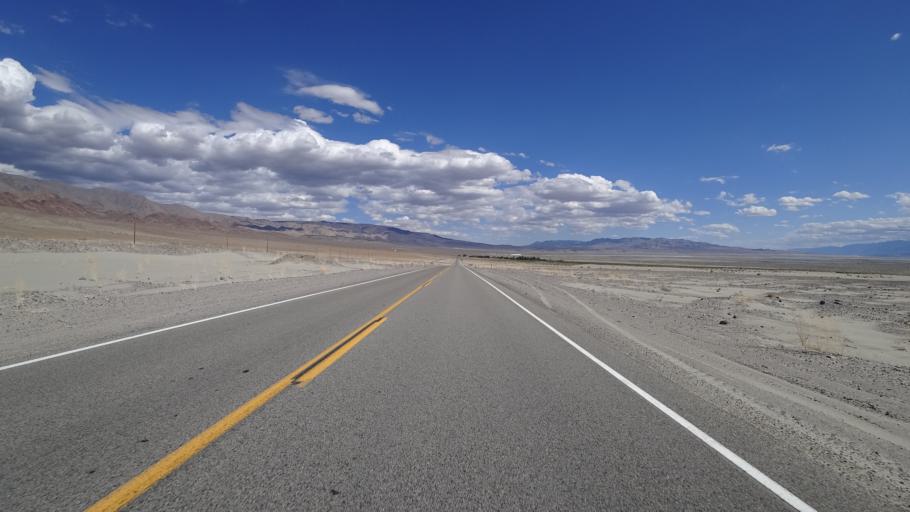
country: US
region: California
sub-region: Inyo County
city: Lone Pine
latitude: 36.5030
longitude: -117.8855
